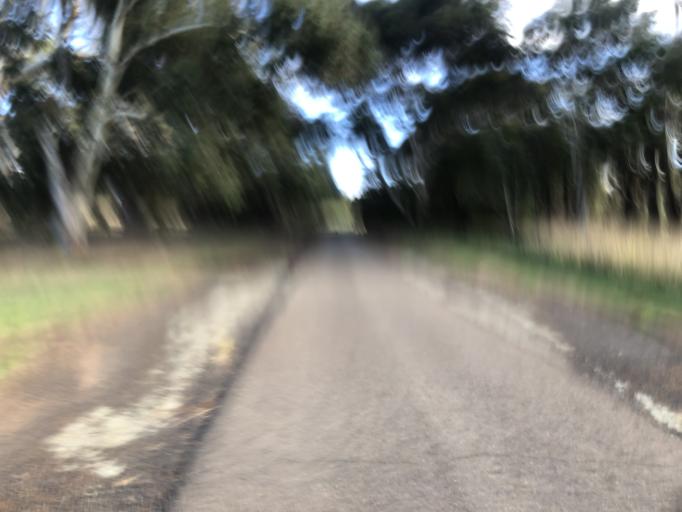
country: AU
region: New South Wales
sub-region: Orange Municipality
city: Orange
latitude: -33.3241
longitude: 149.0861
